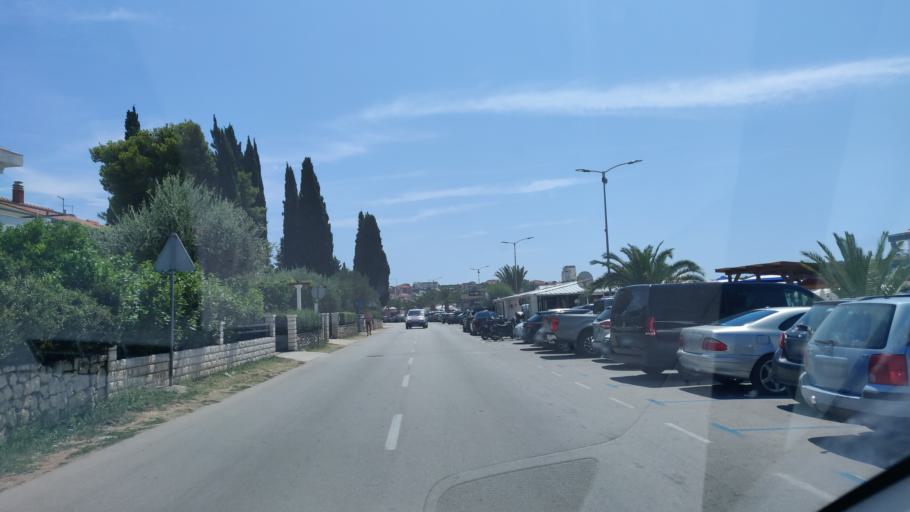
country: HR
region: Splitsko-Dalmatinska
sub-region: Grad Trogir
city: Trogir
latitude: 43.5013
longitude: 16.2592
